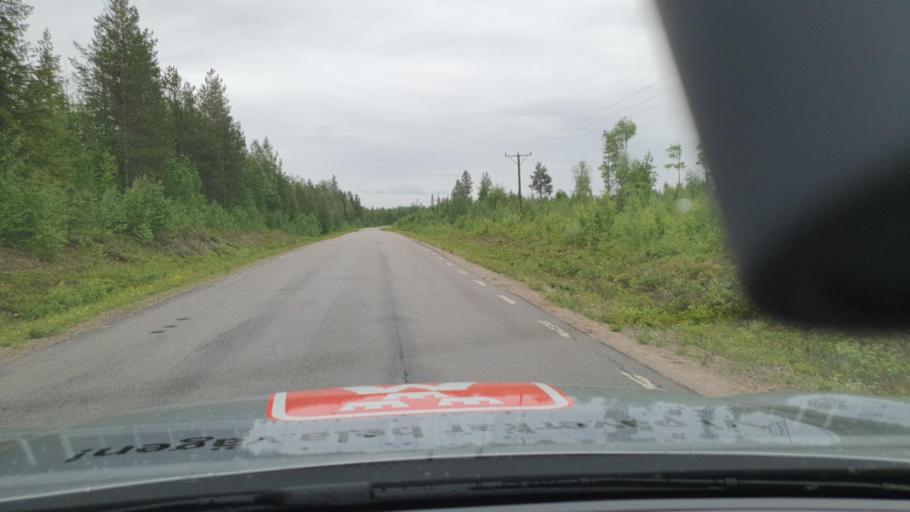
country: SE
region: Norrbotten
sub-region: Pajala Kommun
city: Pajala
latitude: 66.7492
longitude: 23.1651
